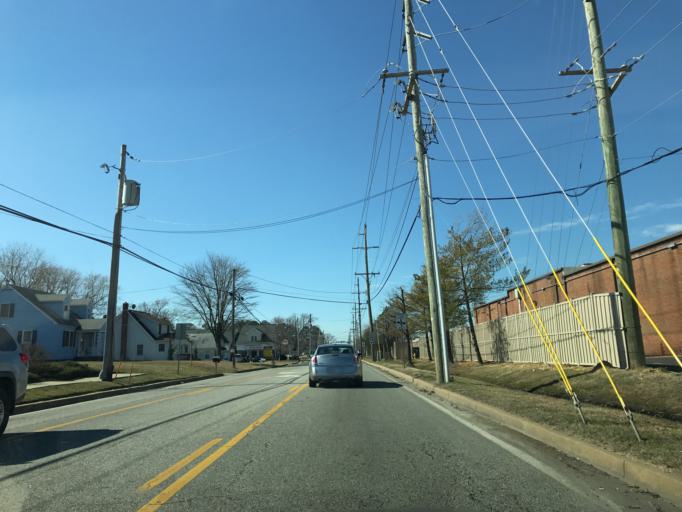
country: US
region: Maryland
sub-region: Queen Anne's County
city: Chester
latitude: 38.9736
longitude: -76.2770
